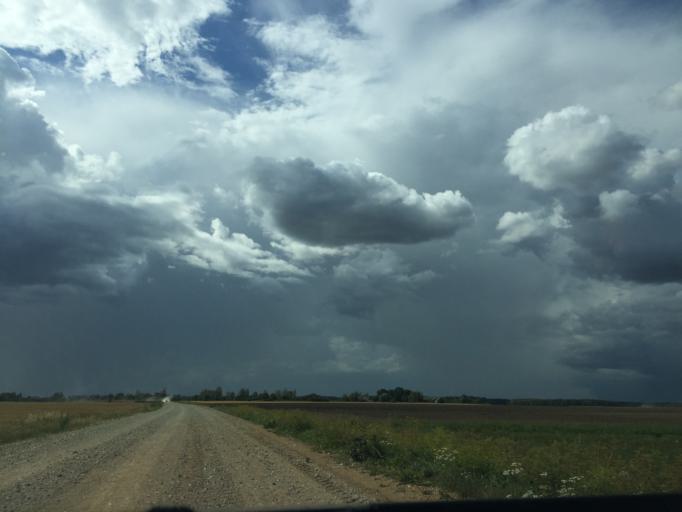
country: LT
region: Siauliu apskritis
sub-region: Joniskis
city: Joniskis
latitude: 56.3737
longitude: 23.5718
